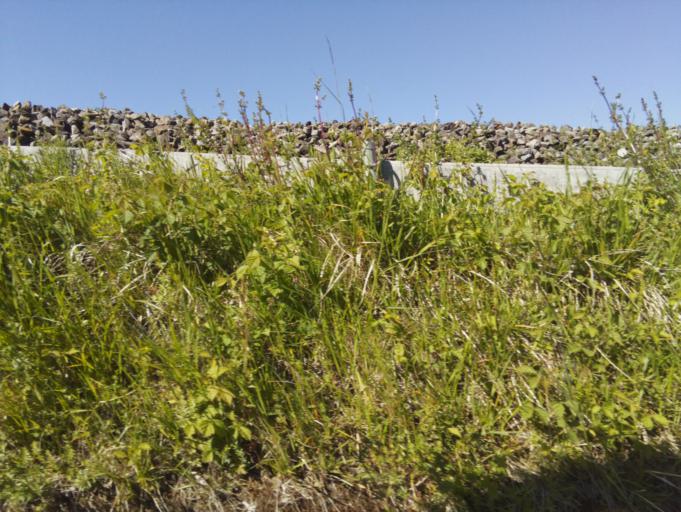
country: CH
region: Schwyz
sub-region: Bezirk March
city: Lachen
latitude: 47.2184
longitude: 8.8711
